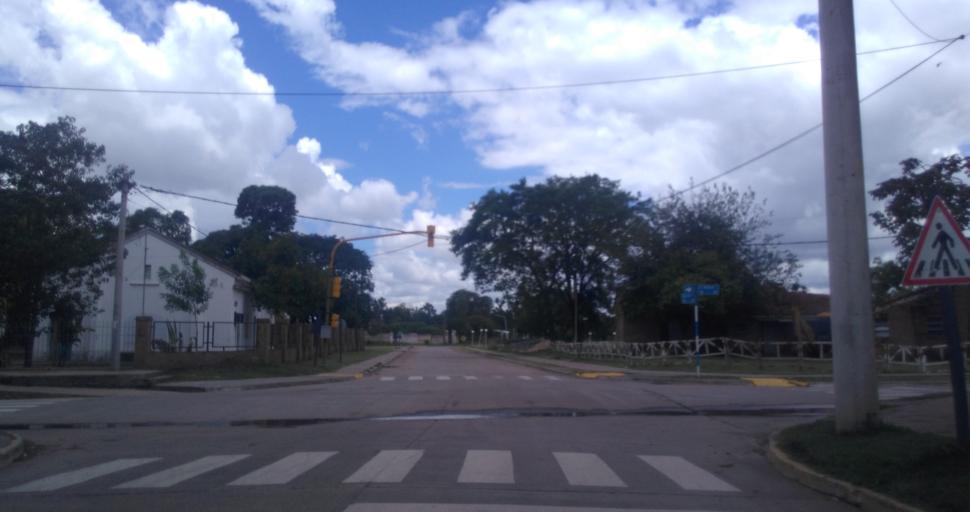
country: AR
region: Chaco
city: Fontana
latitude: -27.4163
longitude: -59.0307
